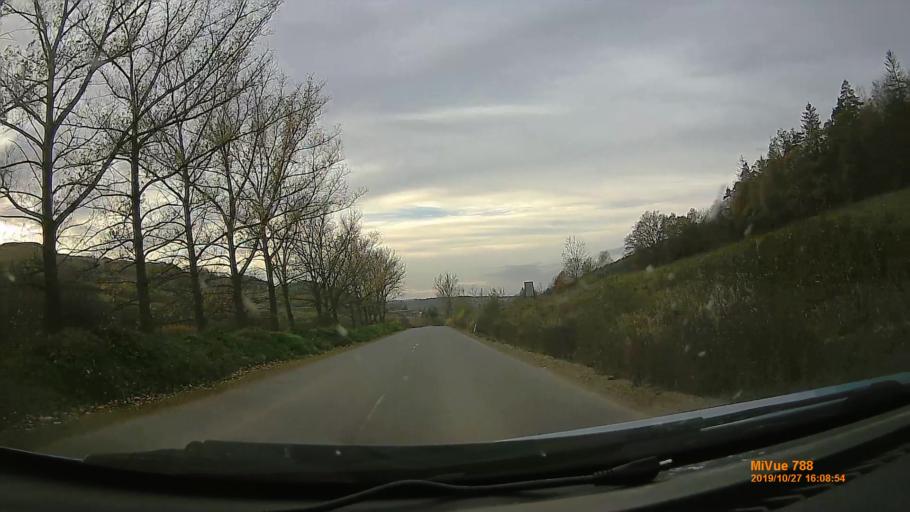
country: PL
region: Lower Silesian Voivodeship
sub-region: Powiat klodzki
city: Nowa Ruda
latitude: 50.5494
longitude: 16.4548
